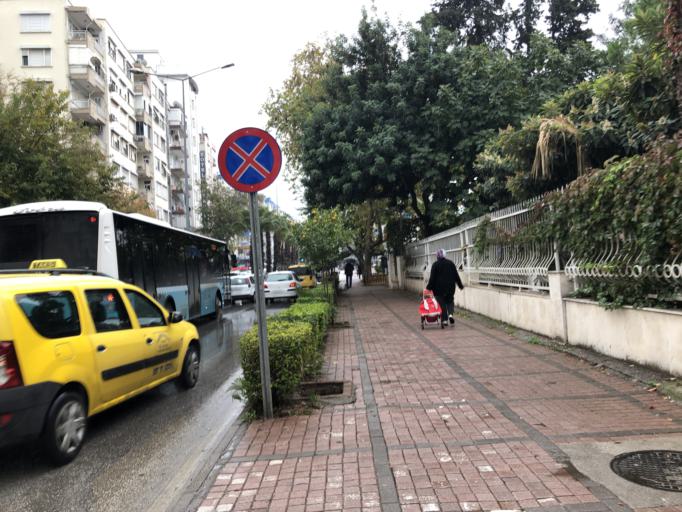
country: TR
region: Antalya
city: Antalya
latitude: 36.8919
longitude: 30.6942
